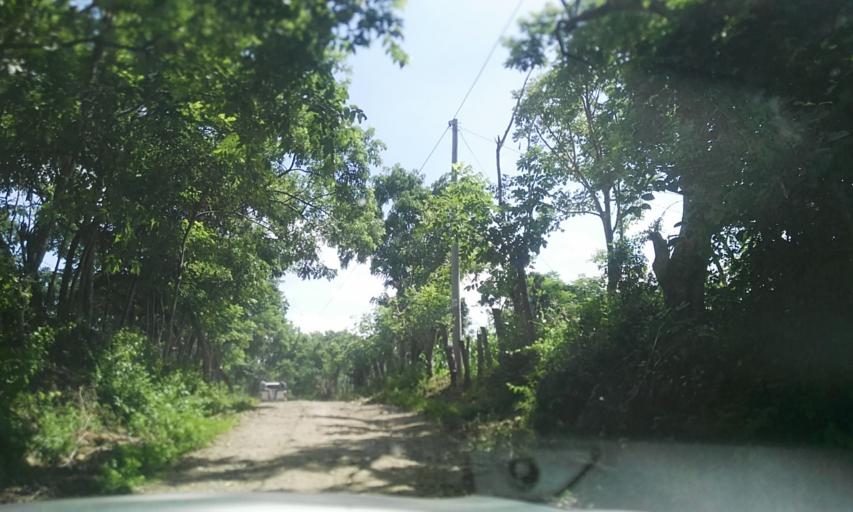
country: NI
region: Matagalpa
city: Terrabona
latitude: 12.6984
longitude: -85.9290
